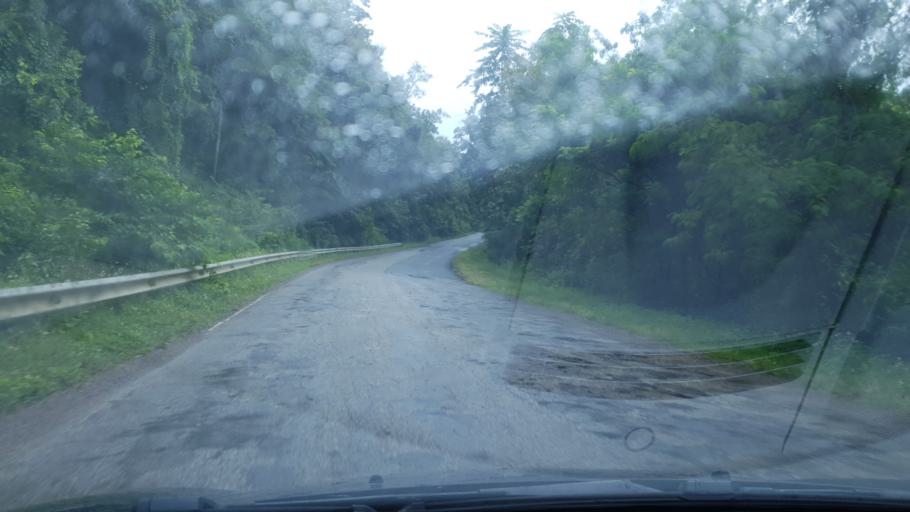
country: TH
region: Mae Hong Son
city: Pa Pae
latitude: 18.2746
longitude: 97.9388
